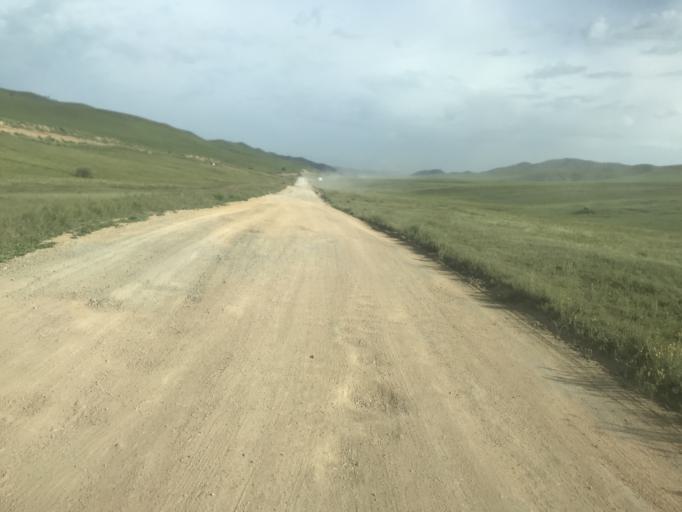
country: MN
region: Central Aimak
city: Javhlant
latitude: 48.7406
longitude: 106.1287
